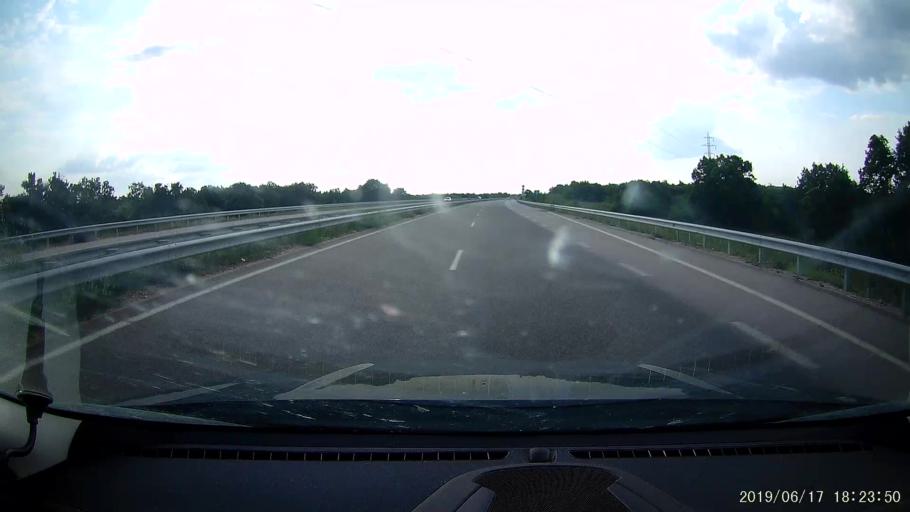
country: BG
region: Khaskovo
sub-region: Obshtina Dimitrovgrad
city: Dimitrovgrad
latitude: 41.9779
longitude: 25.7090
